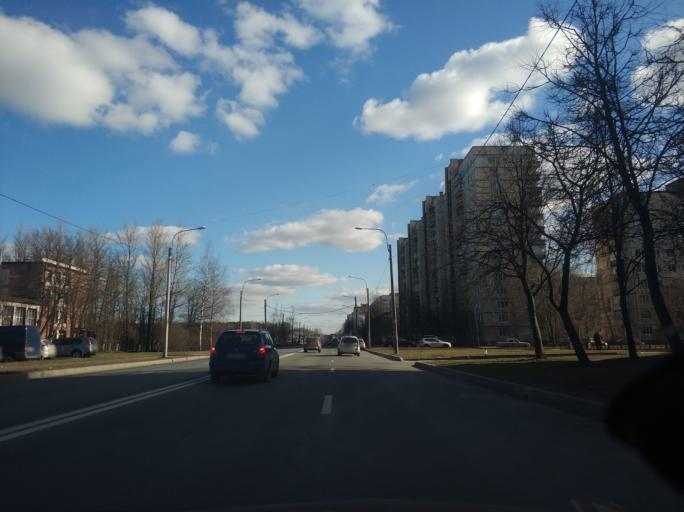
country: RU
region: St.-Petersburg
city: Krasnogvargeisky
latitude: 59.9556
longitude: 30.4952
